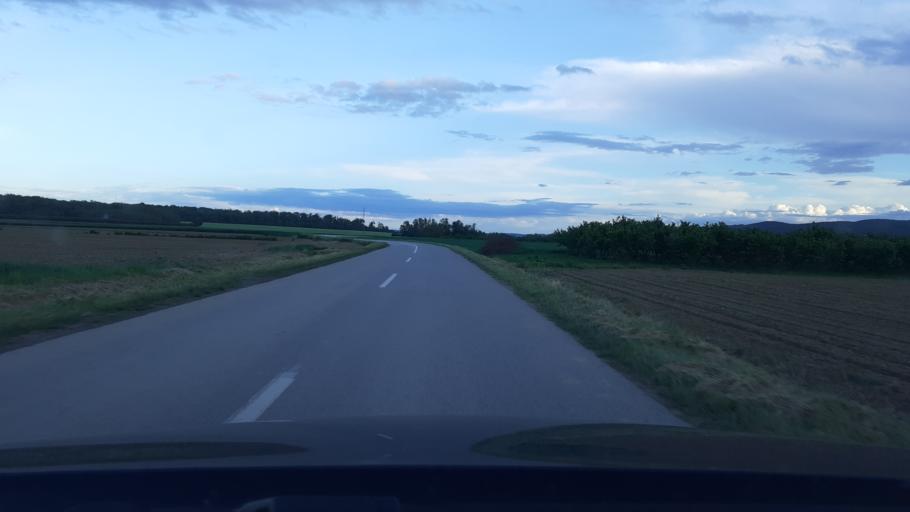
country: HR
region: Pozesko-Slavonska
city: Jaksic
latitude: 45.3560
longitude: 17.7752
